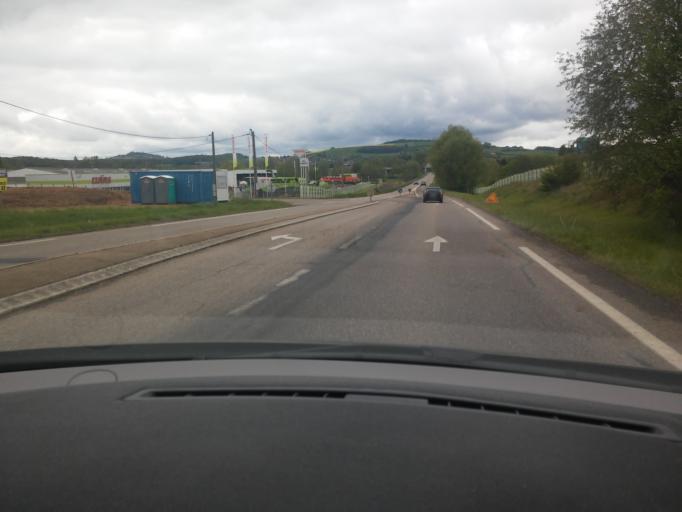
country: FR
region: Lorraine
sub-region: Departement de Meurthe-et-Moselle
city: Pont-a-Mousson
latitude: 48.9429
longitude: 6.1319
